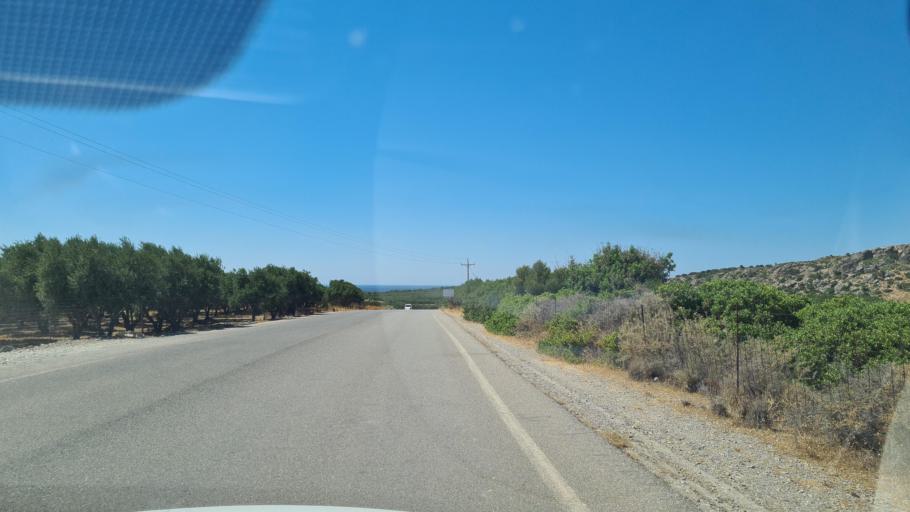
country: GR
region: Crete
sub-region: Nomos Chanias
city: Palaiochora
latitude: 35.2933
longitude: 23.5439
